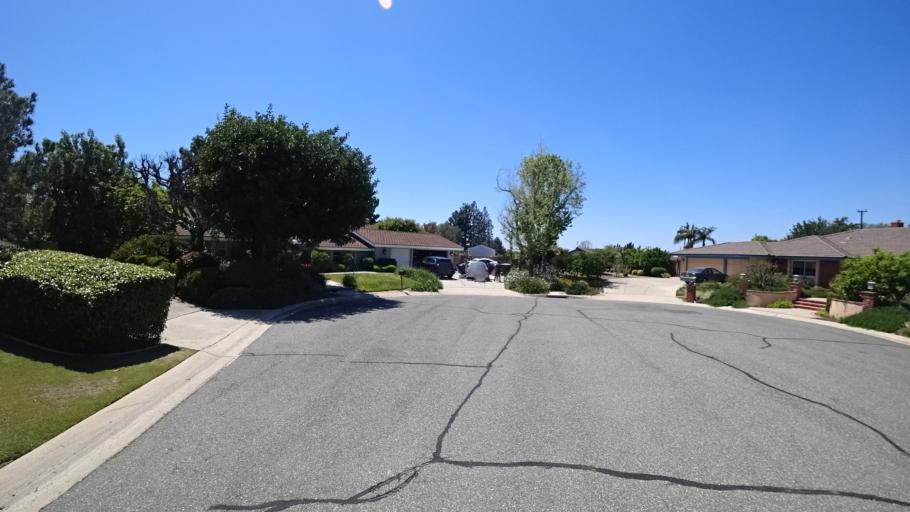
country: US
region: California
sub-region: Orange County
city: Villa Park
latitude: 33.8210
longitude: -117.8152
